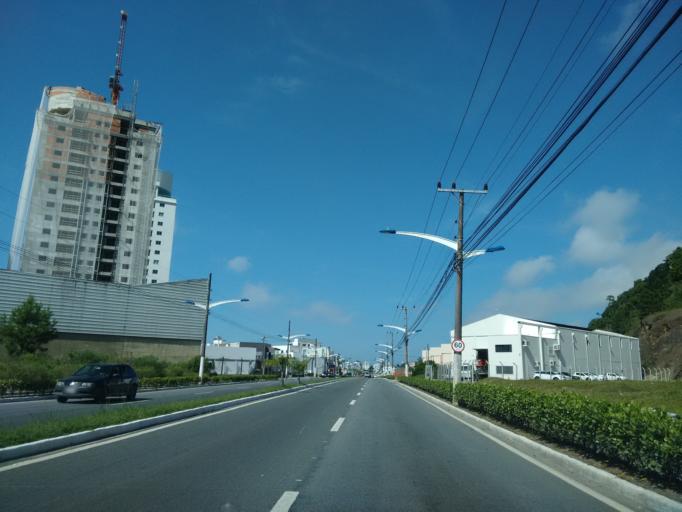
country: BR
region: Santa Catarina
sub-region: Itajai
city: Itajai
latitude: -26.9278
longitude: -48.6823
